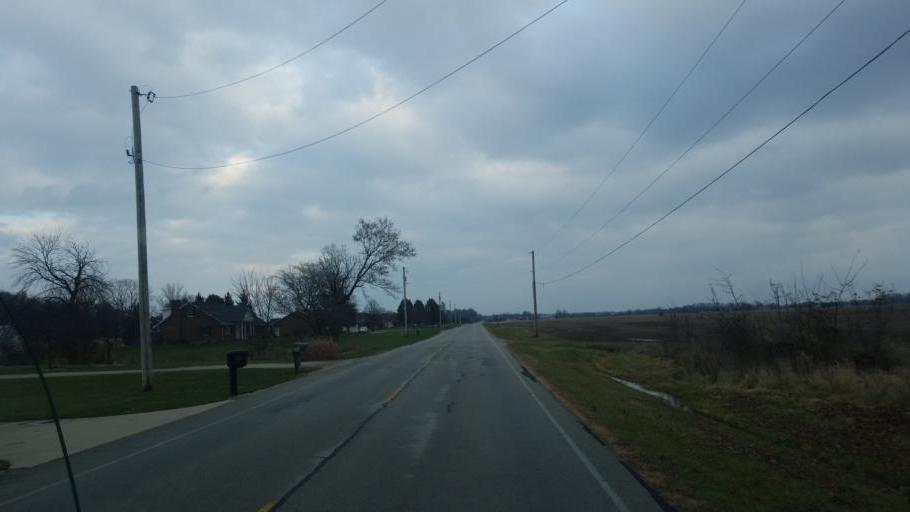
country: US
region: Ohio
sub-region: Mercer County
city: Coldwater
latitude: 40.5089
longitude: -84.6242
